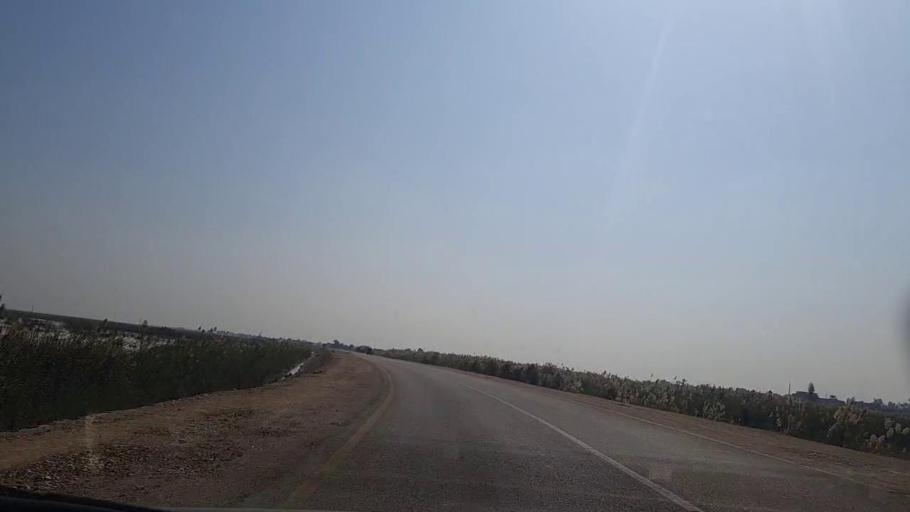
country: PK
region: Sindh
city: Sakrand
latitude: 26.0812
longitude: 68.4026
